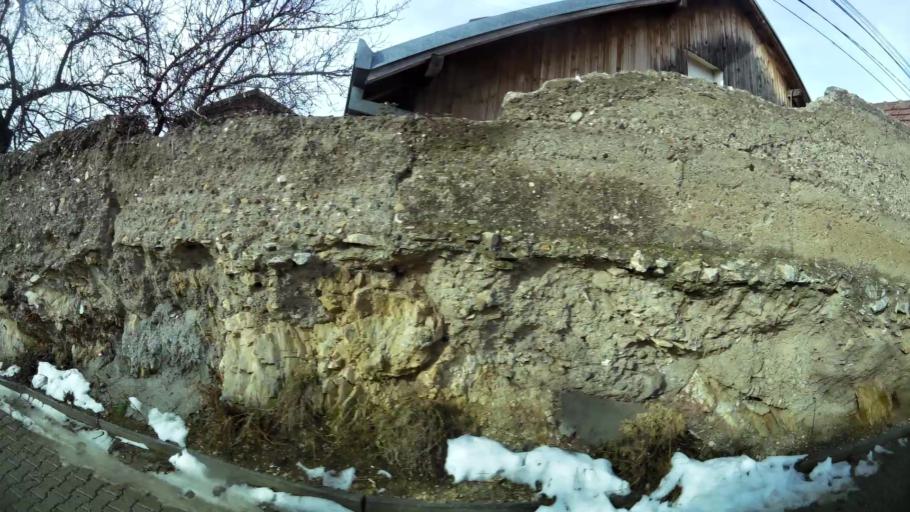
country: XK
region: Pristina
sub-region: Komuna e Prishtines
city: Pristina
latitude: 42.6702
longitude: 21.1766
